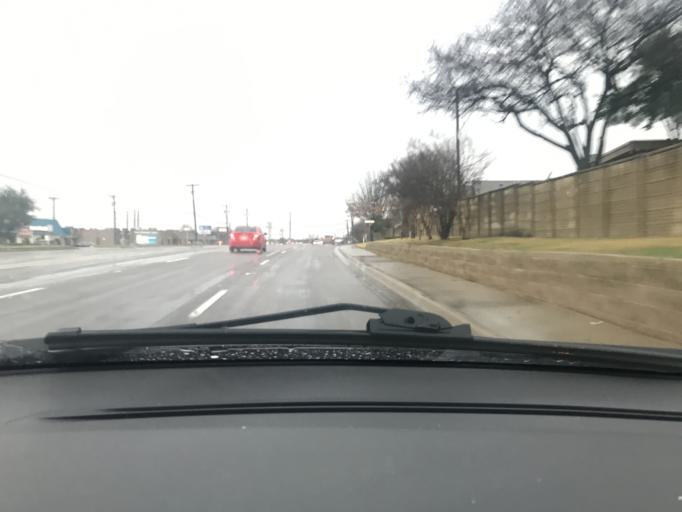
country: US
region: Texas
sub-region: Tarrant County
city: Bedford
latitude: 32.8527
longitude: -97.1616
